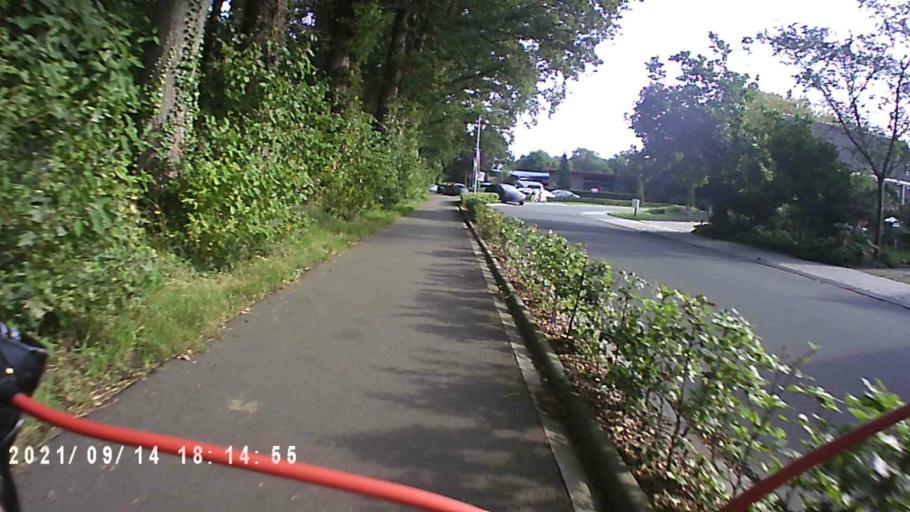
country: NL
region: Drenthe
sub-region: Gemeente Tynaarlo
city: Zuidlaren
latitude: 53.0850
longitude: 6.6700
